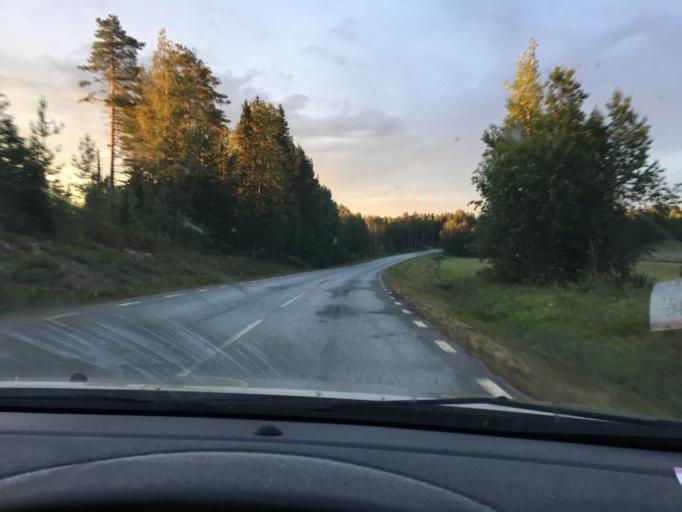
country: SE
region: Norrbotten
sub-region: Kalix Kommun
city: Toere
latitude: 66.0672
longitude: 22.6834
